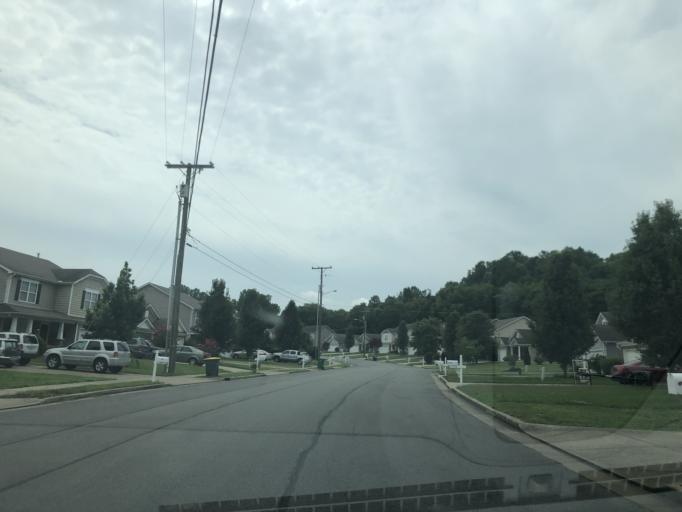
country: US
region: Tennessee
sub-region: Williamson County
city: Nolensville
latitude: 36.0204
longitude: -86.6736
